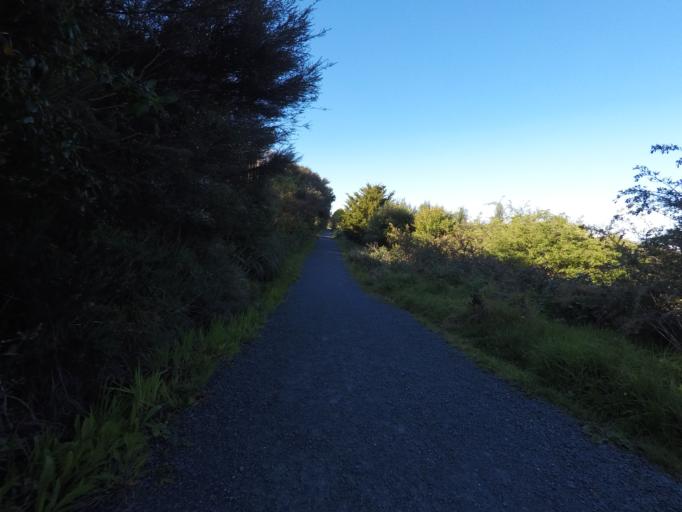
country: NZ
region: Auckland
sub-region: Auckland
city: Rosebank
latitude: -36.8436
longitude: 174.6568
